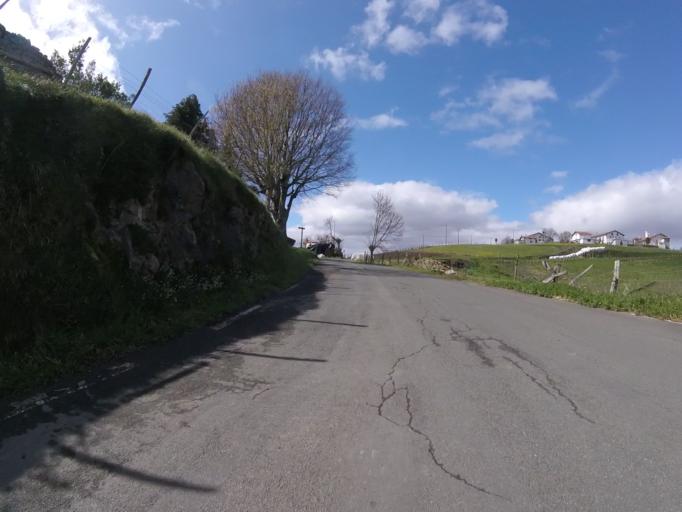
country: ES
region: Basque Country
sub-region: Provincia de Guipuzcoa
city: Tolosa
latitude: 43.1334
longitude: -2.1049
